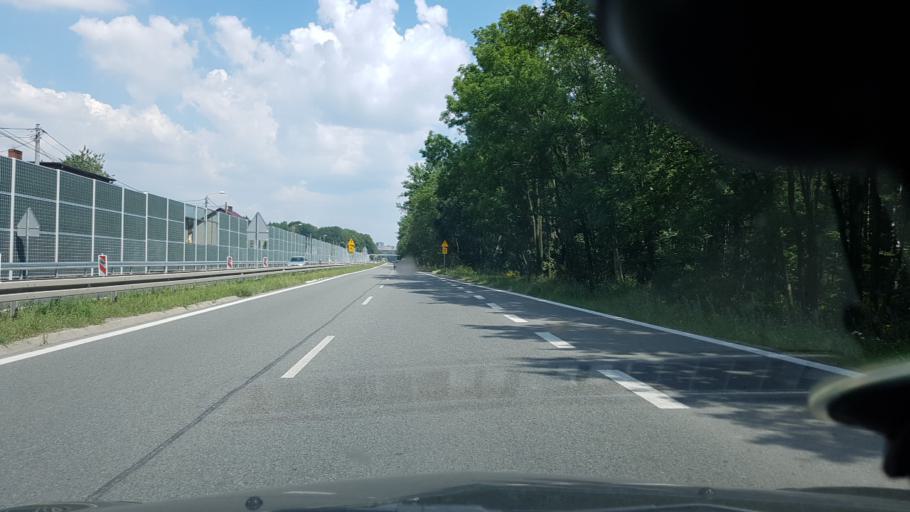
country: PL
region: Silesian Voivodeship
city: Gardawice
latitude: 50.1229
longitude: 18.8169
